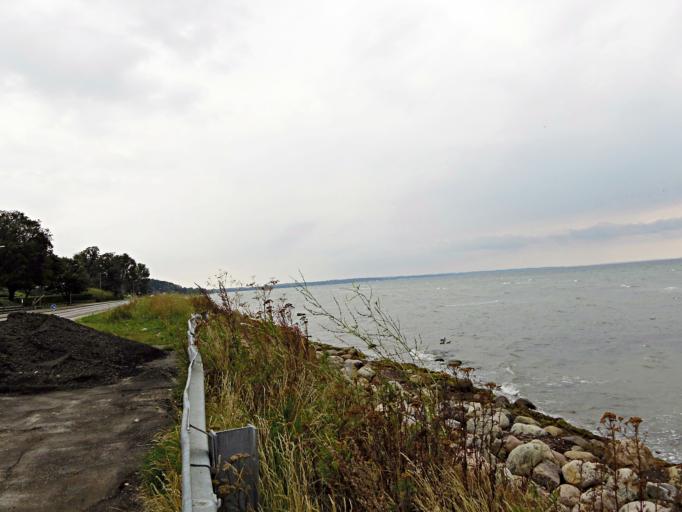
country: DK
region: Capital Region
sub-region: Horsholm Kommune
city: Horsholm
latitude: 55.8976
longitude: 12.5355
